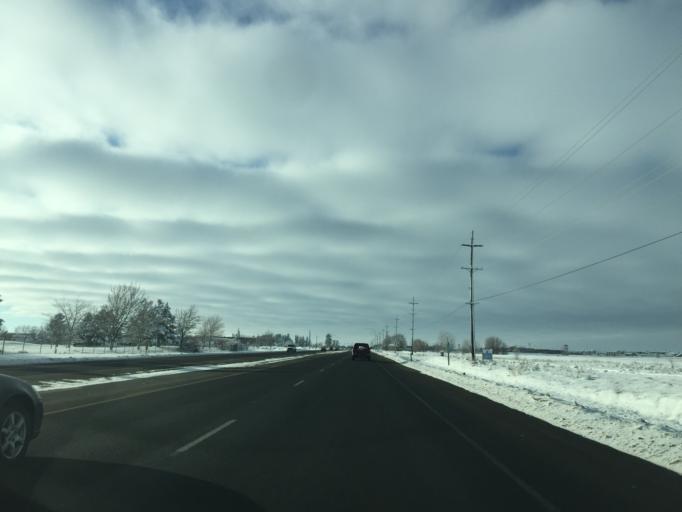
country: US
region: Washington
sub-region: Spokane County
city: Airway Heights
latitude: 47.6433
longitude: -117.5436
